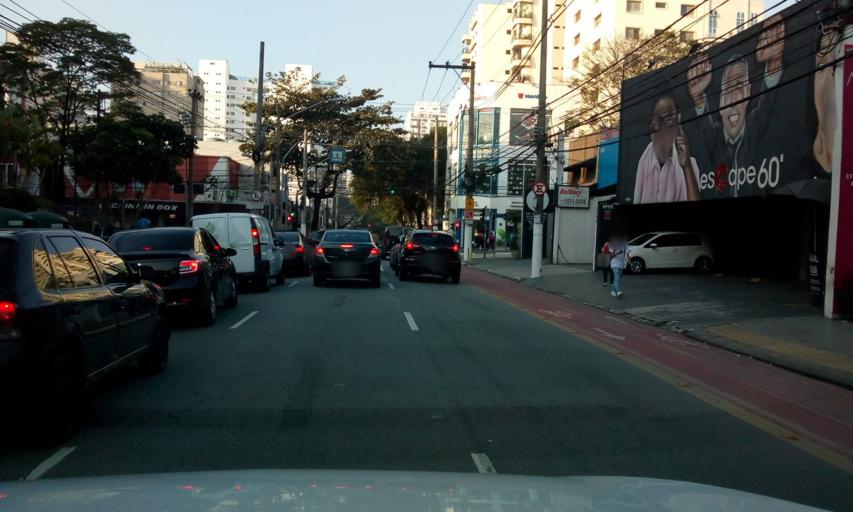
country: BR
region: Sao Paulo
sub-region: Sao Paulo
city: Sao Paulo
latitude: -23.6106
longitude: -46.6658
